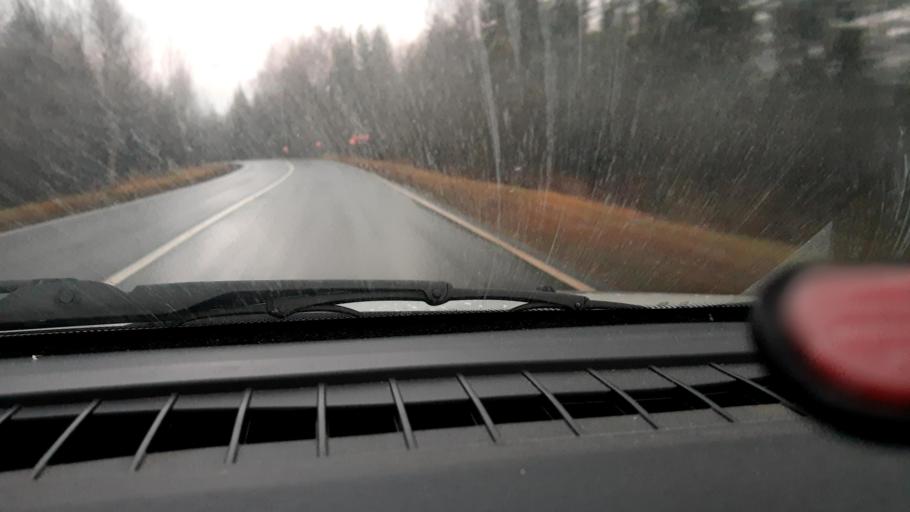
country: RU
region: Nizjnij Novgorod
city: Uren'
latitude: 57.2476
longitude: 45.5989
